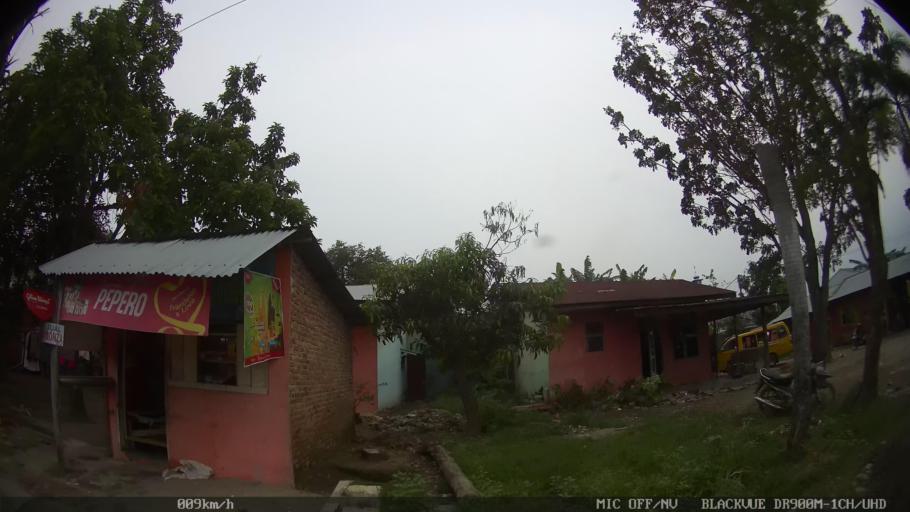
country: ID
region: North Sumatra
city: Medan
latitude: 3.5736
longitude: 98.7334
